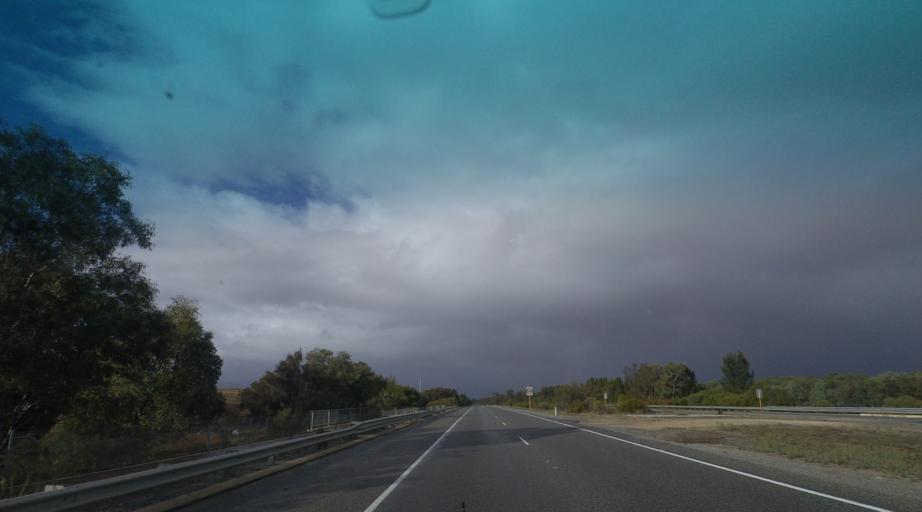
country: AU
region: Western Australia
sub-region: Serpentine-Jarrahdale
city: Oakford
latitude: -32.1925
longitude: 115.9625
